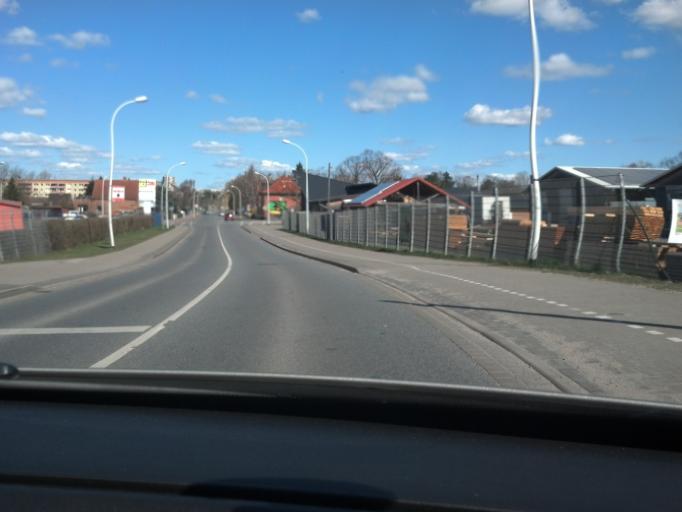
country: DE
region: Mecklenburg-Vorpommern
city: Neubrandenburg
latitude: 53.5593
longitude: 13.2832
